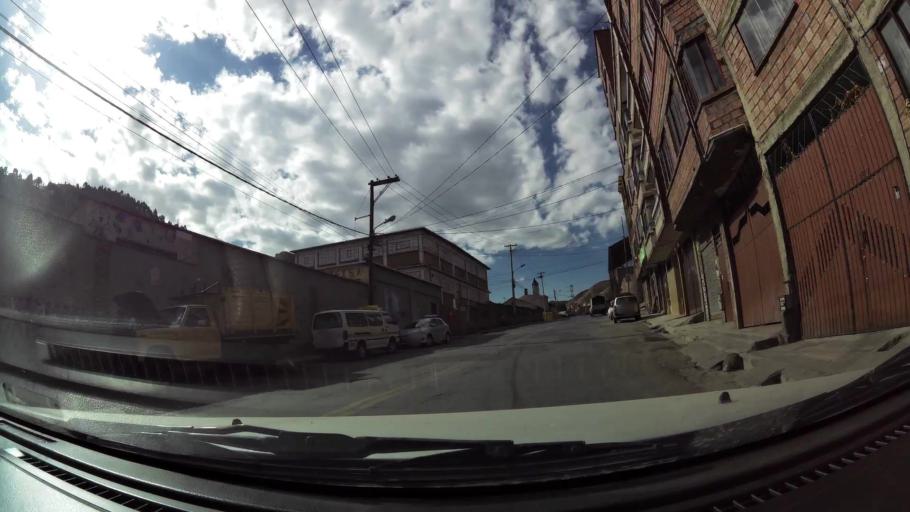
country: BO
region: La Paz
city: La Paz
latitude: -16.4675
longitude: -68.1519
